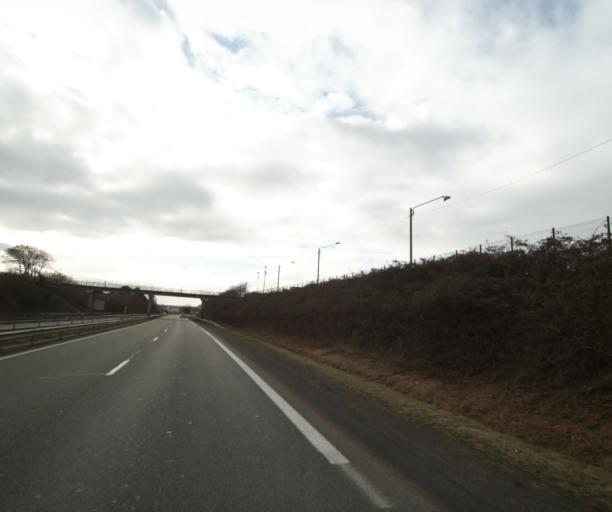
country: FR
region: Pays de la Loire
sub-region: Departement de la Sarthe
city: Le Mans
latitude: 47.9601
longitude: 0.2128
